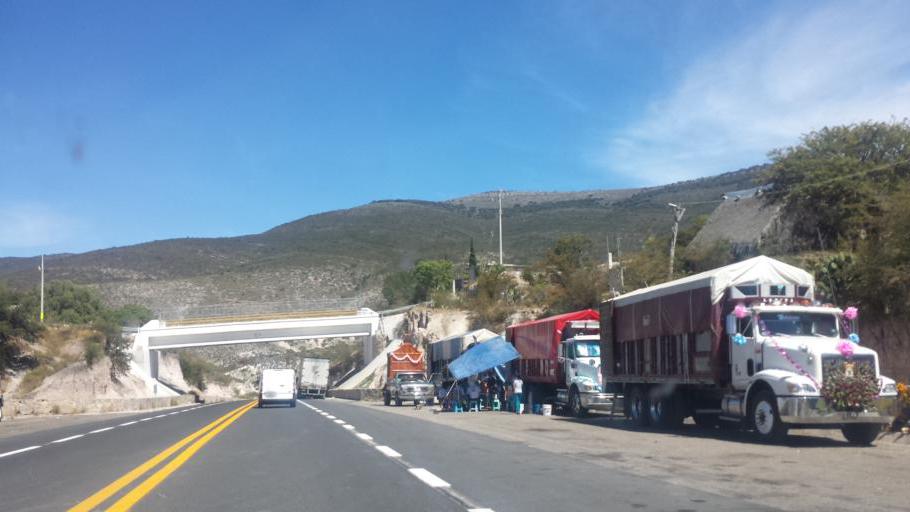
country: MX
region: Oaxaca
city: San Gabriel Casa Blanca
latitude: 17.9793
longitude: -97.3560
